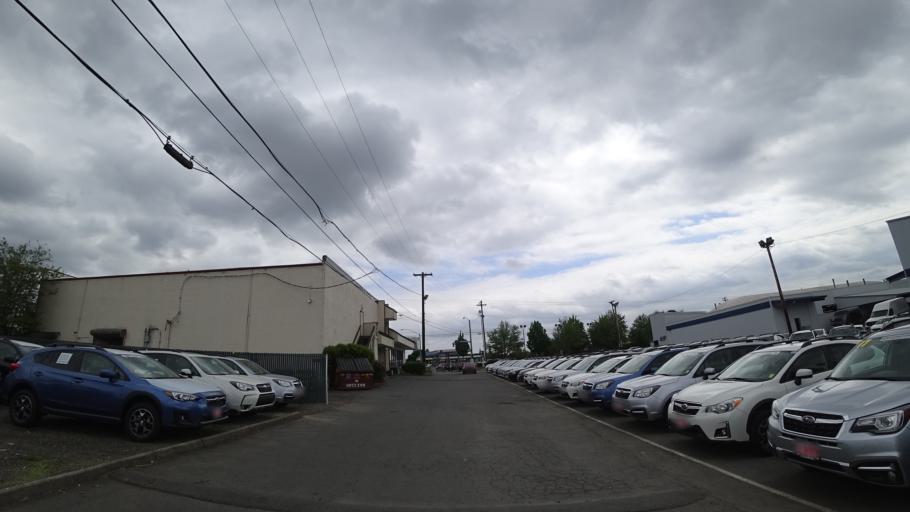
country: US
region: Oregon
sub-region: Washington County
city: Beaverton
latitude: 45.4908
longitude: -122.7957
